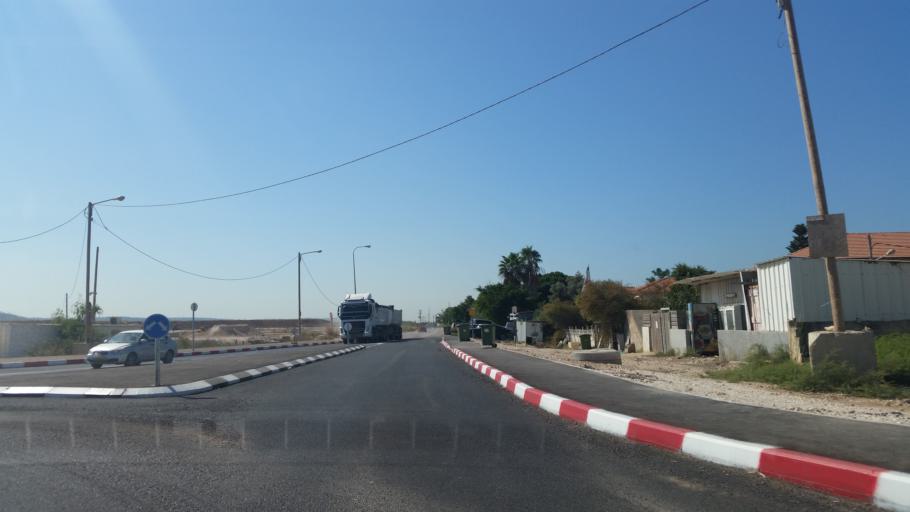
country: IL
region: Haifa
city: `Atlit
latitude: 32.6875
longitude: 34.9442
